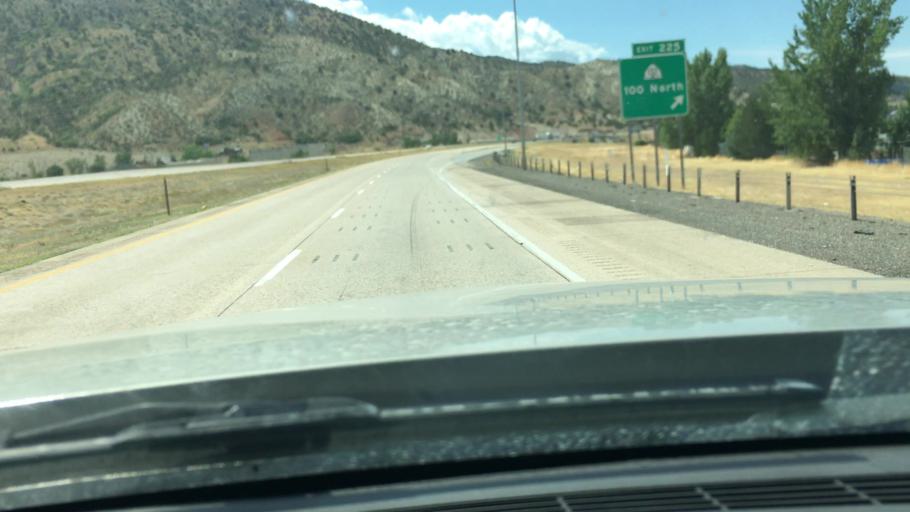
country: US
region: Utah
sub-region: Juab County
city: Nephi
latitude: 39.7159
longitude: -111.8175
